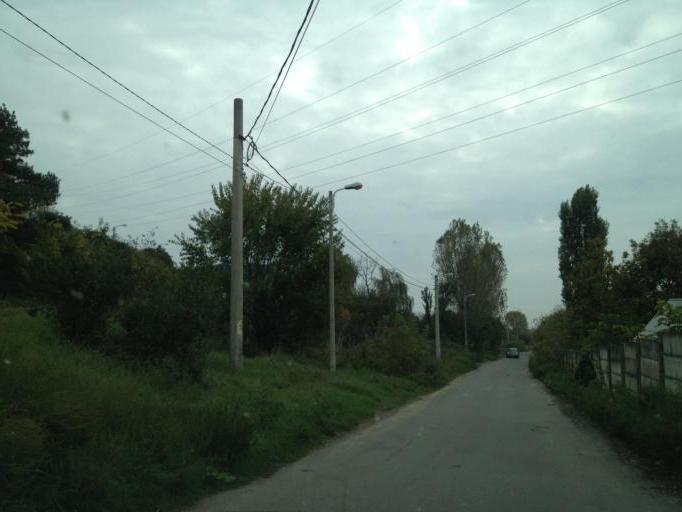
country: RO
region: Dolj
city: Craiova
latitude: 44.2953
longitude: 23.8038
